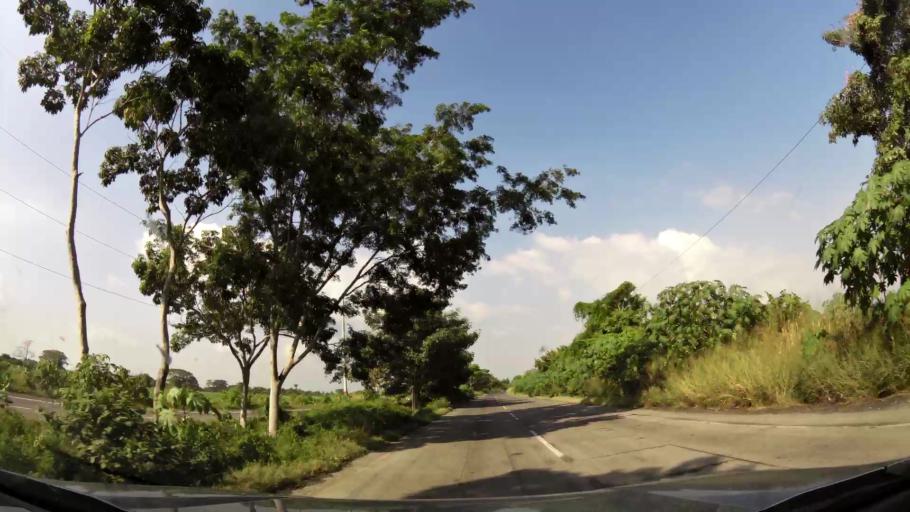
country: GT
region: Escuintla
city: Puerto San Jose
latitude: 13.9970
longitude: -90.7878
